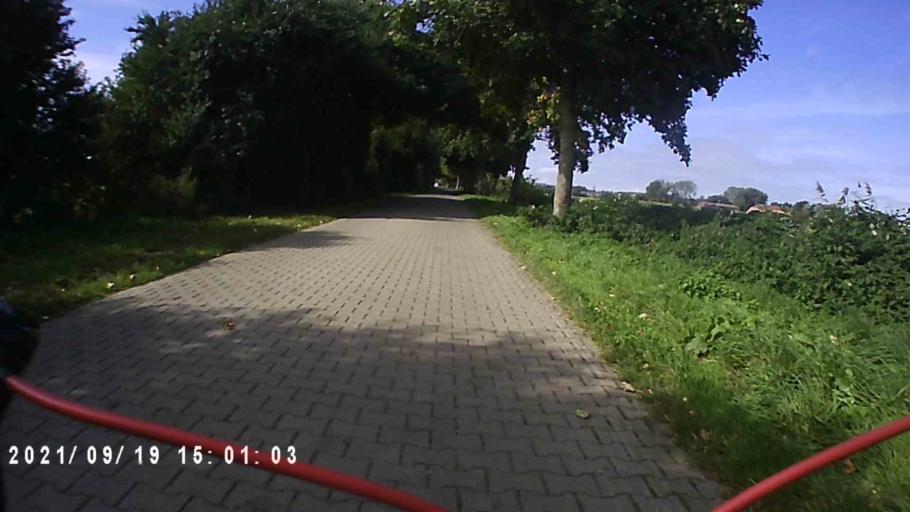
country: DE
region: Lower Saxony
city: Bunde
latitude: 53.1580
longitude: 7.2065
